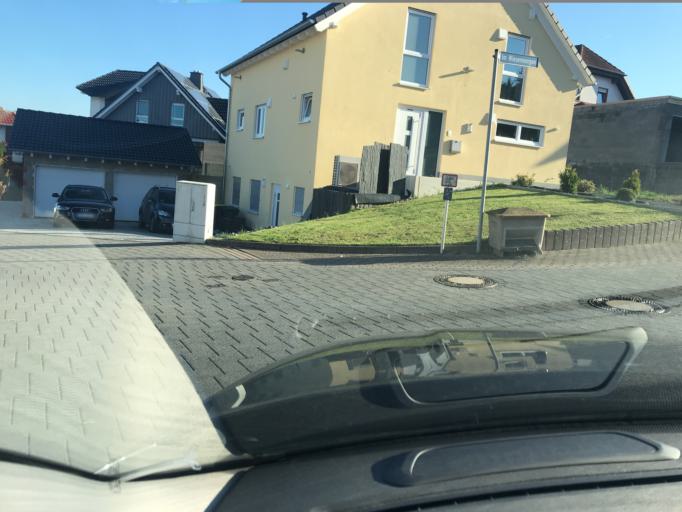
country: DE
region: Rheinland-Pfalz
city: Eppenrod
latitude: 50.4243
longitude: 7.9353
